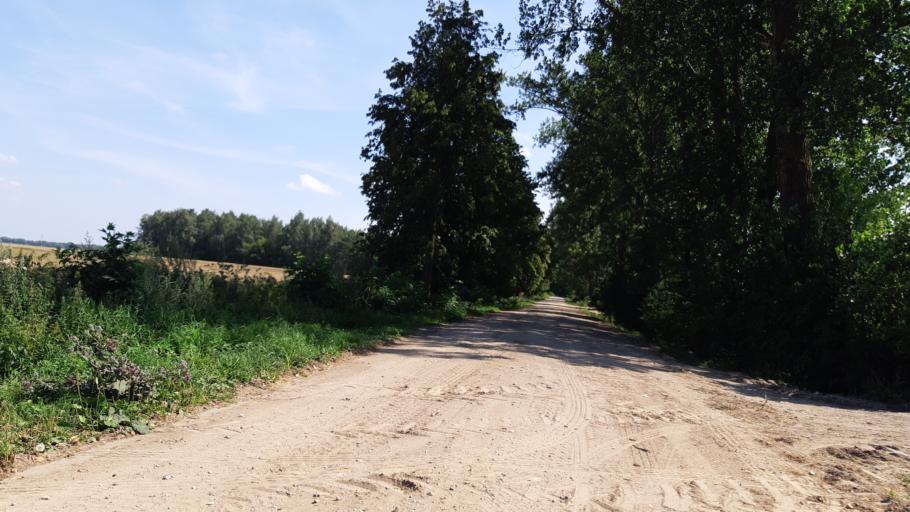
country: LT
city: Virbalis
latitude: 54.6377
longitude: 22.8233
